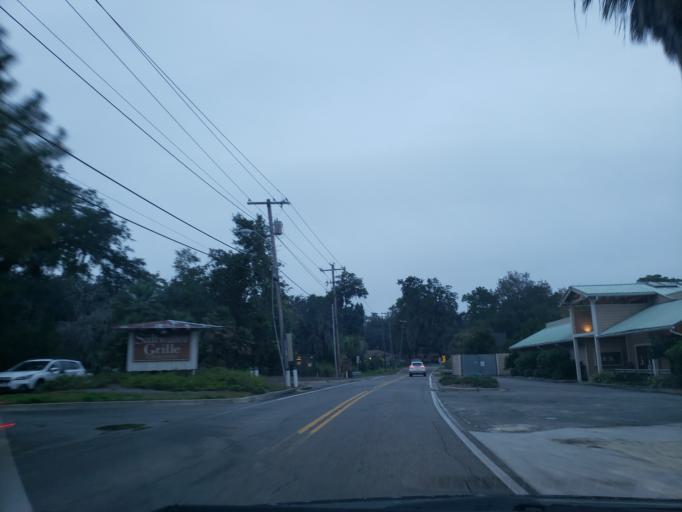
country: US
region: Georgia
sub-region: Chatham County
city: Isle of Hope
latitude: 31.9995
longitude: -81.0636
